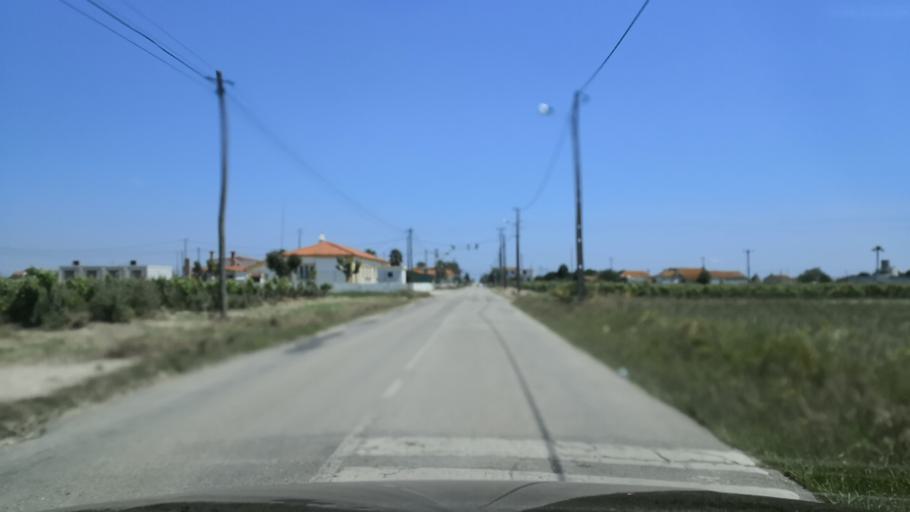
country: PT
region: Setubal
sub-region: Palmela
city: Palmela
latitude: 38.6034
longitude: -8.8189
